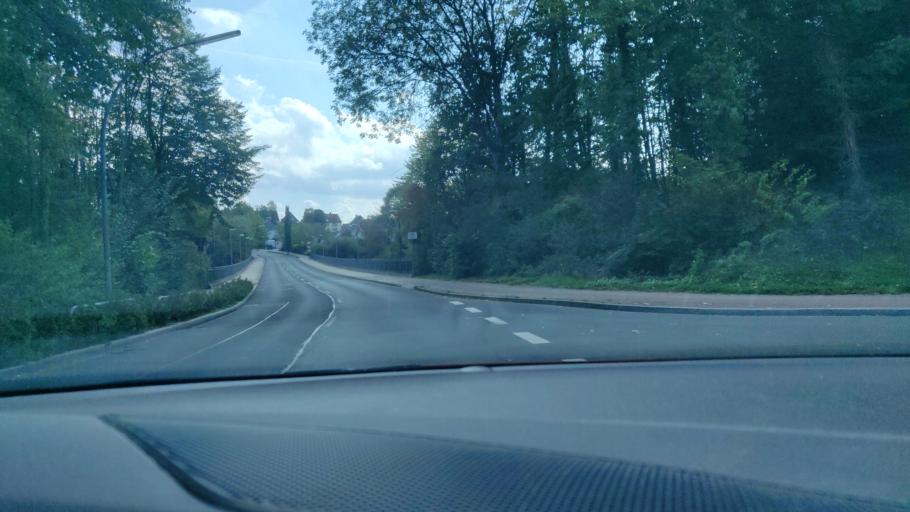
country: DE
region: North Rhine-Westphalia
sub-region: Regierungsbezirk Dusseldorf
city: Velbert
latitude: 51.3516
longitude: 7.0354
